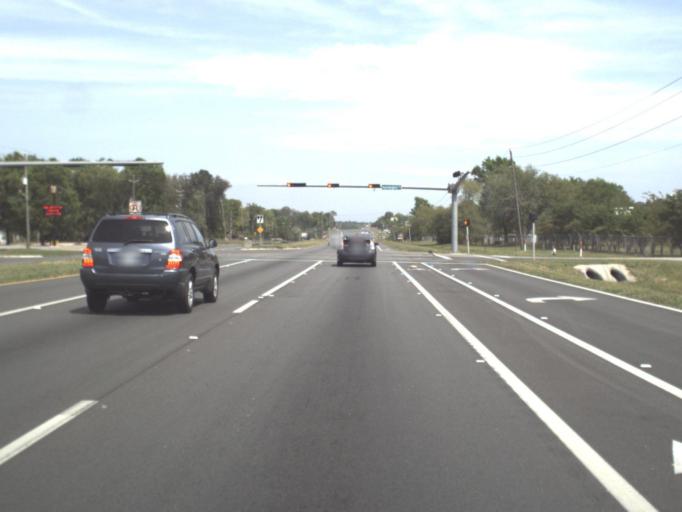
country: US
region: Florida
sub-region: Escambia County
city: Ensley
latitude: 30.5327
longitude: -87.2547
